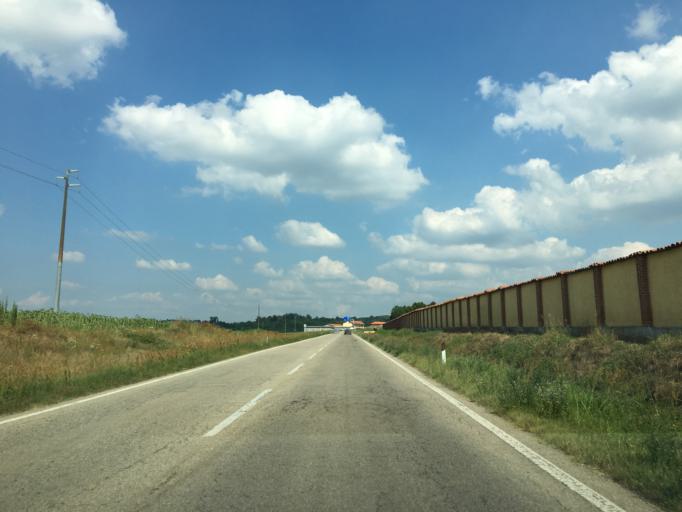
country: IT
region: Piedmont
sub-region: Provincia di Cuneo
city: Ceresole Alba
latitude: 44.7845
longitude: 7.8570
